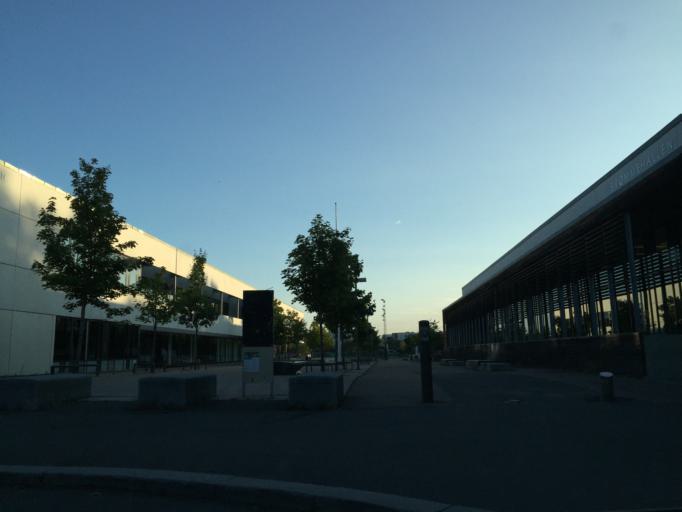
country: NO
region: Akershus
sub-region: Baerum
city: Lysaker
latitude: 59.8898
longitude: 10.6211
